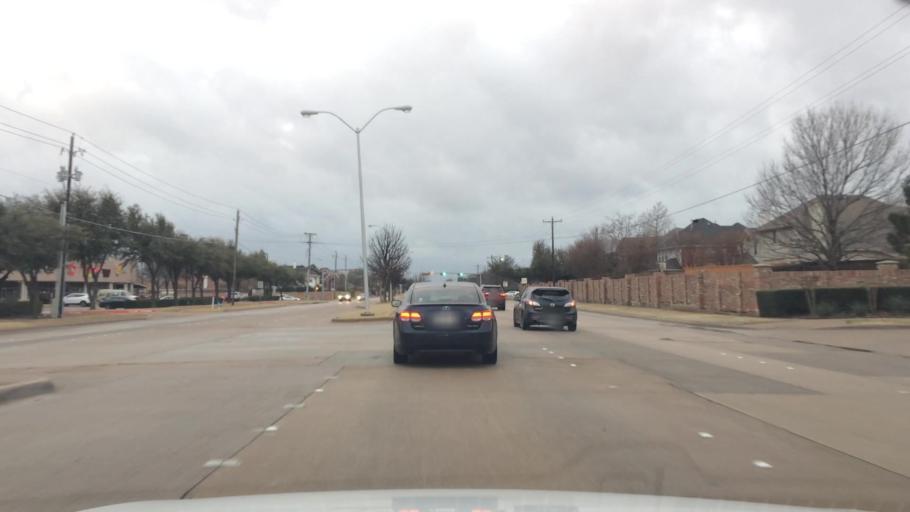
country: US
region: Texas
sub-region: Collin County
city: Frisco
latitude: 33.0877
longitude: -96.7717
